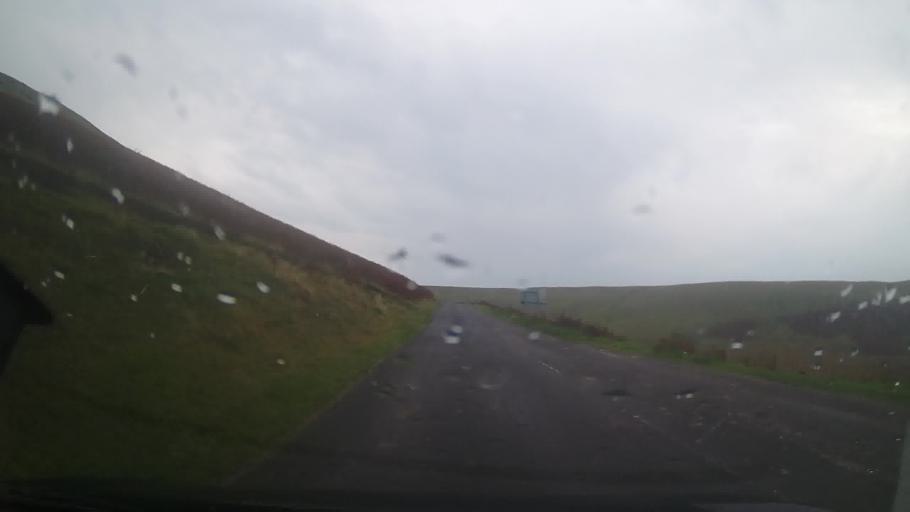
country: GB
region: Wales
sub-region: Sir Powys
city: Rhayader
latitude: 52.3319
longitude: -3.6081
